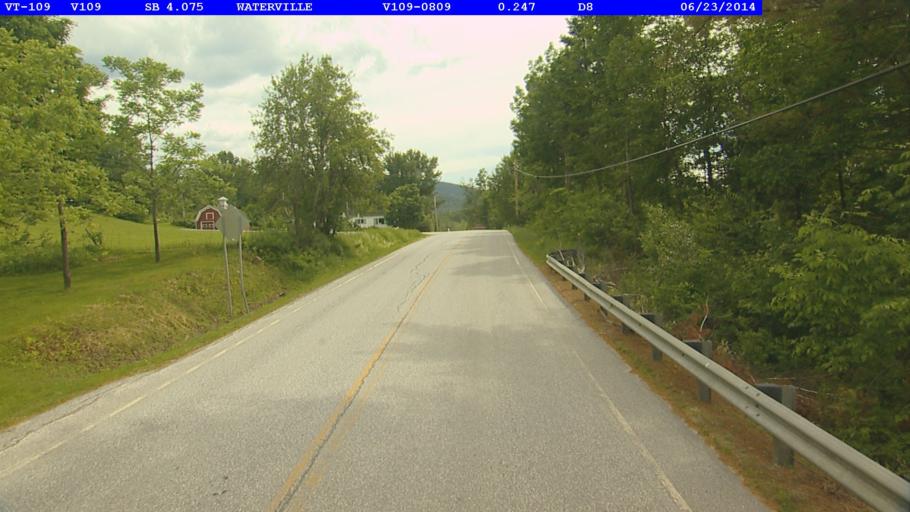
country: US
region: Vermont
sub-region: Lamoille County
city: Johnson
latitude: 44.6861
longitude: -72.7700
